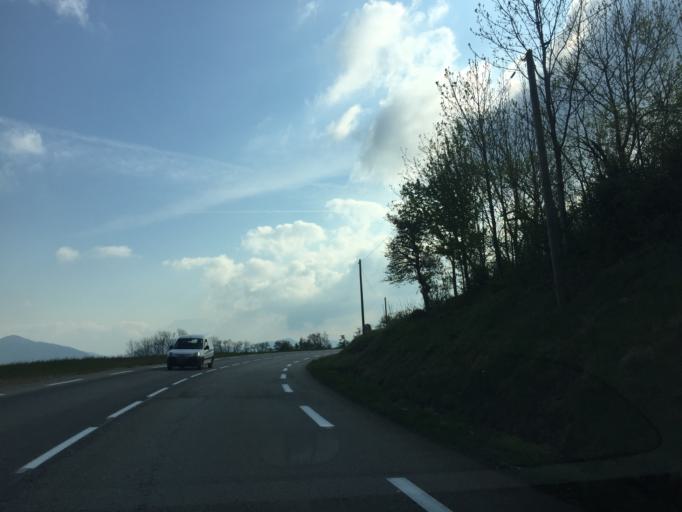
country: FR
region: Rhone-Alpes
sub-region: Departement de l'Isere
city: Mens
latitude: 44.7759
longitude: 5.6546
